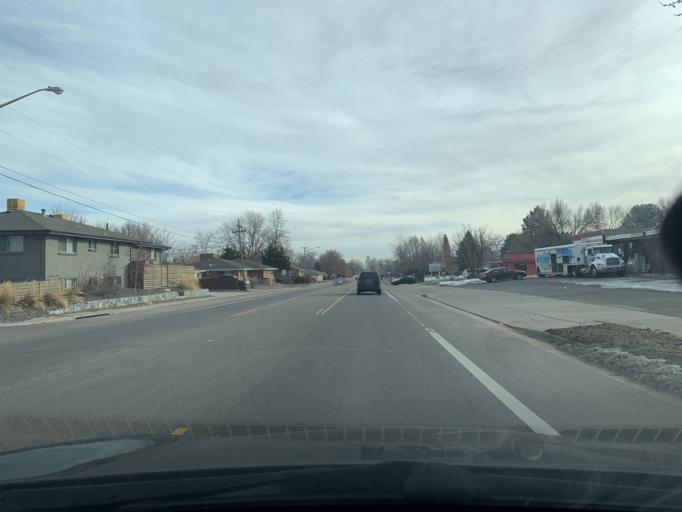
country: US
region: Colorado
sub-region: Jefferson County
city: Edgewater
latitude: 39.7476
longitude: -105.0687
